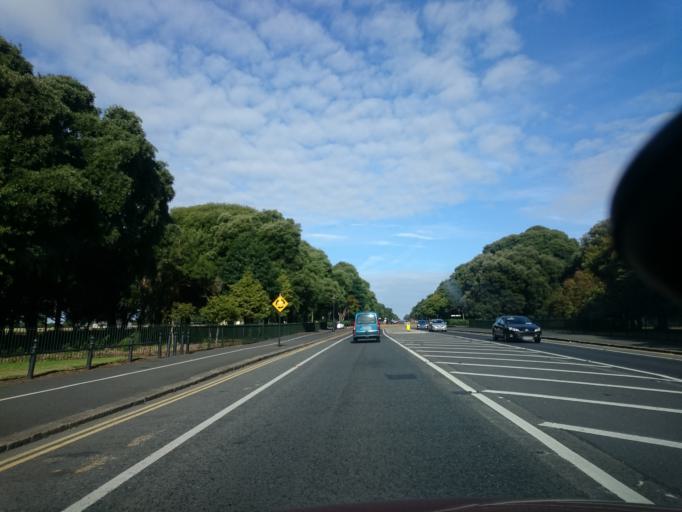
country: IE
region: Leinster
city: Rialto
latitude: 53.3503
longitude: -6.3022
